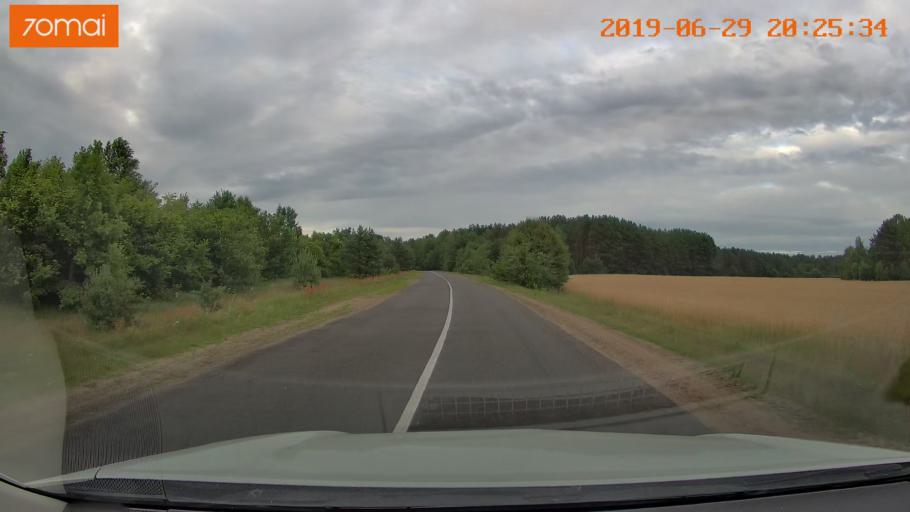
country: BY
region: Brest
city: Asnyezhytsy
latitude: 52.4578
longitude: 26.2824
